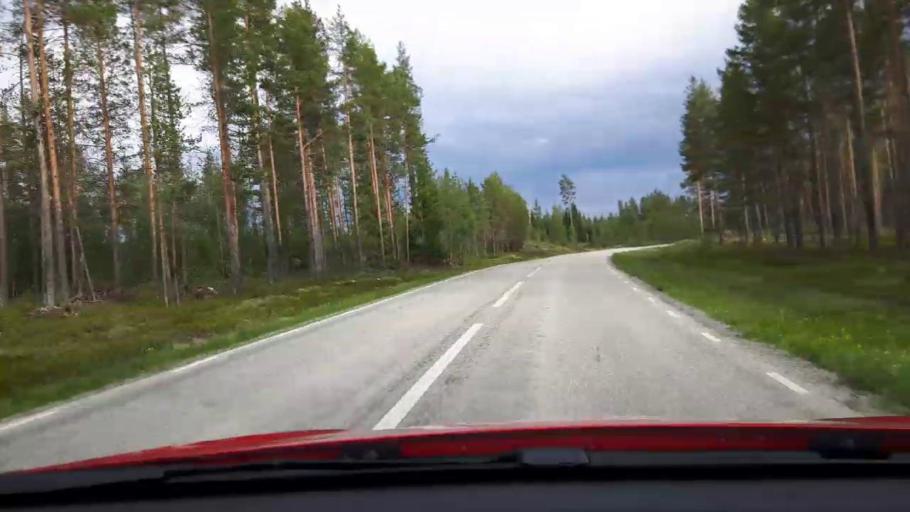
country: SE
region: Jaemtland
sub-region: Bergs Kommun
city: Hoverberg
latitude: 62.6614
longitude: 14.0540
